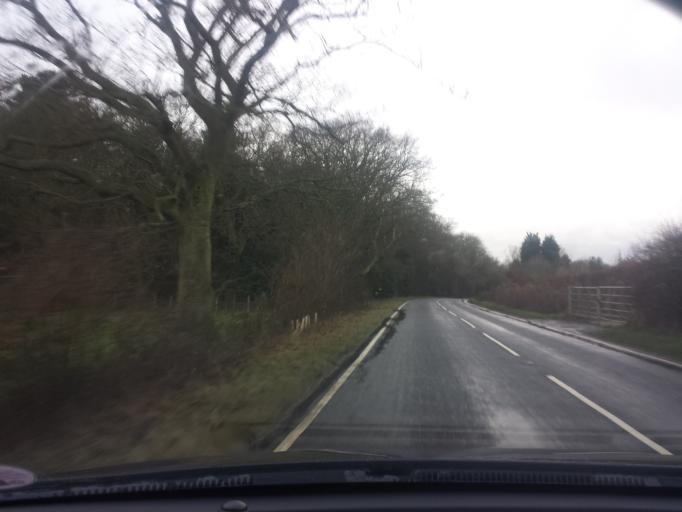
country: GB
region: England
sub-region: Essex
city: Little Clacton
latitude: 51.8734
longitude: 1.1387
